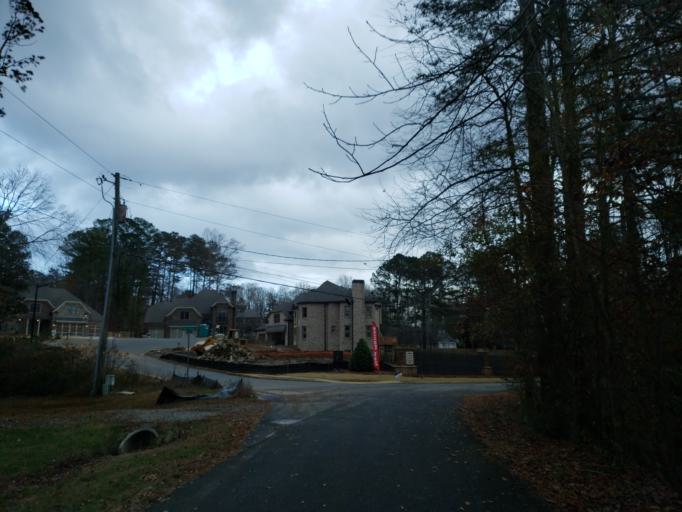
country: US
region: Georgia
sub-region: Cherokee County
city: Woodstock
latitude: 34.0425
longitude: -84.4955
